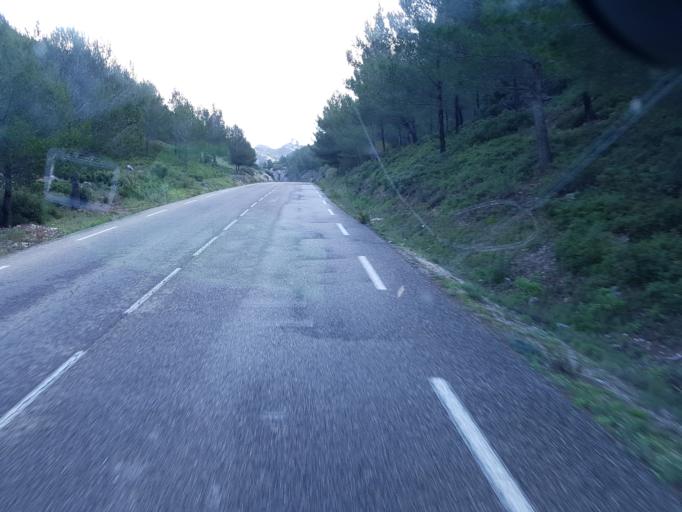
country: FR
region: Provence-Alpes-Cote d'Azur
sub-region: Departement des Bouches-du-Rhone
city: Le Rove
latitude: 43.3508
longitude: 5.2388
